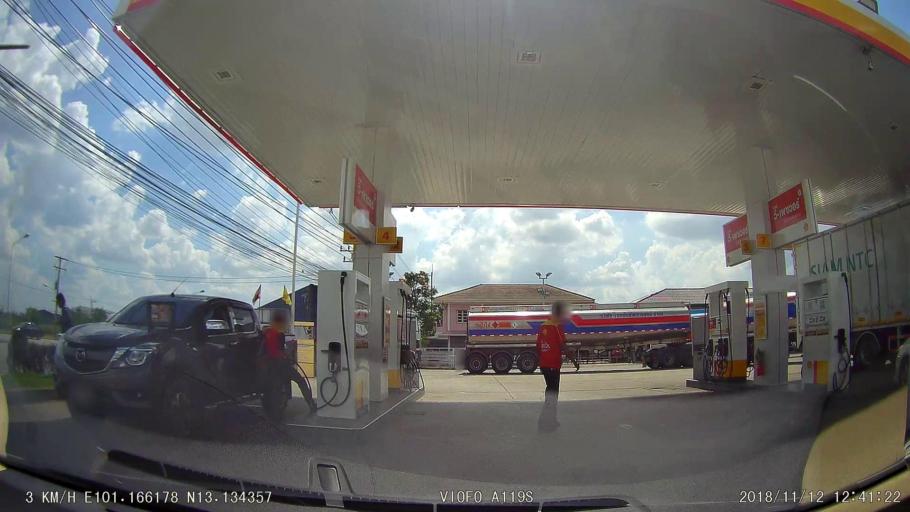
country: TH
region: Rayong
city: Pluak Daeng
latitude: 13.1397
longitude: 101.1657
